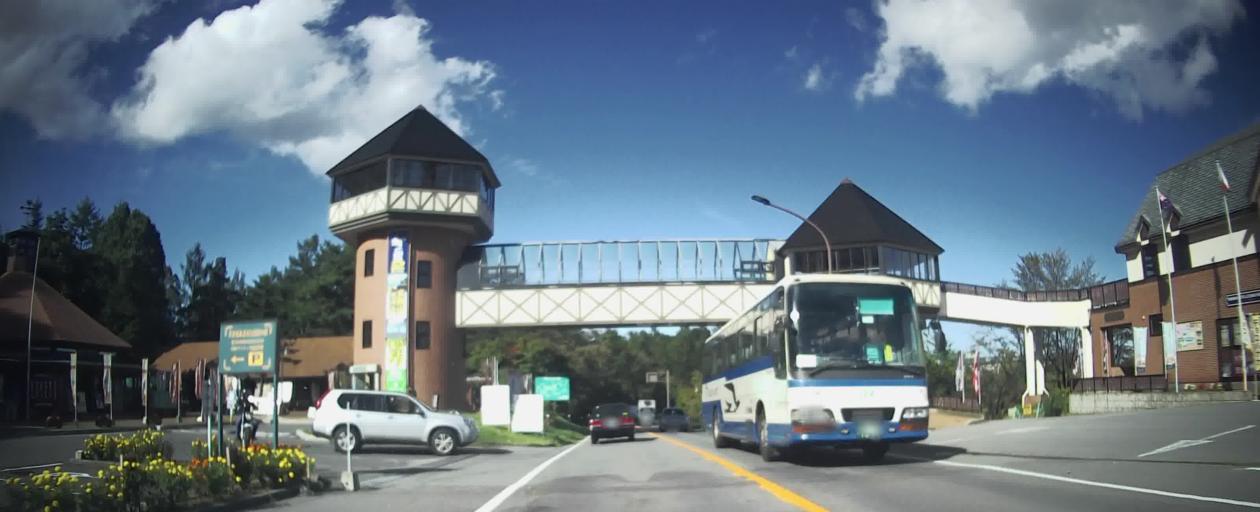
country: JP
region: Gunma
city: Nakanojomachi
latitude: 36.6147
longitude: 138.5903
